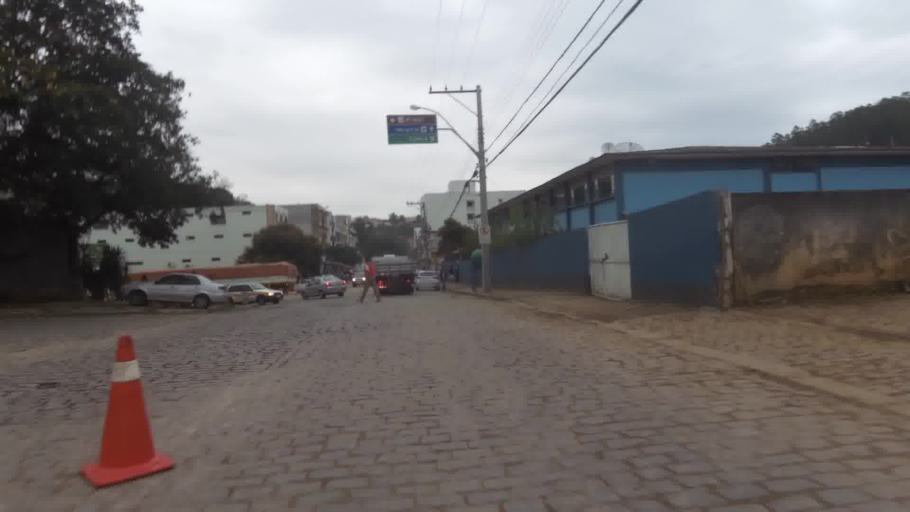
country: BR
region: Espirito Santo
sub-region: Iconha
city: Iconha
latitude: -20.7892
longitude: -40.8162
